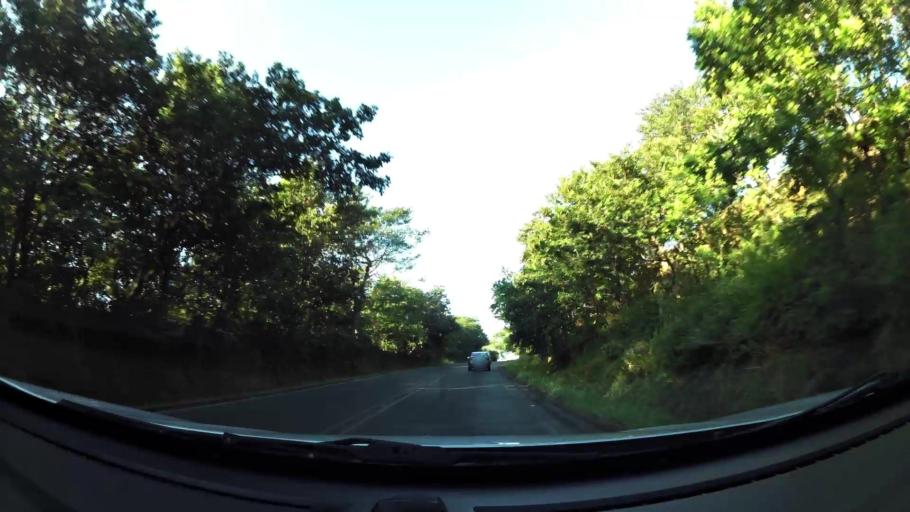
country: CR
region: Puntarenas
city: Miramar
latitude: 10.0965
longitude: -84.8153
